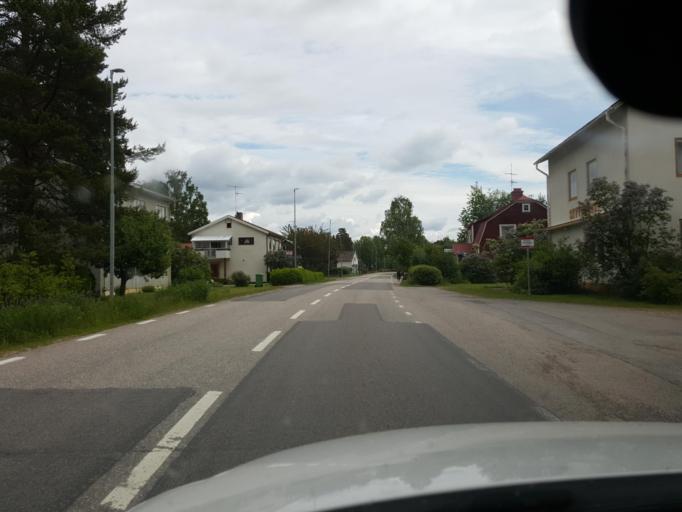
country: SE
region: Gaevleborg
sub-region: Ljusdals Kommun
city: Farila
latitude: 61.8110
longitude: 15.7531
